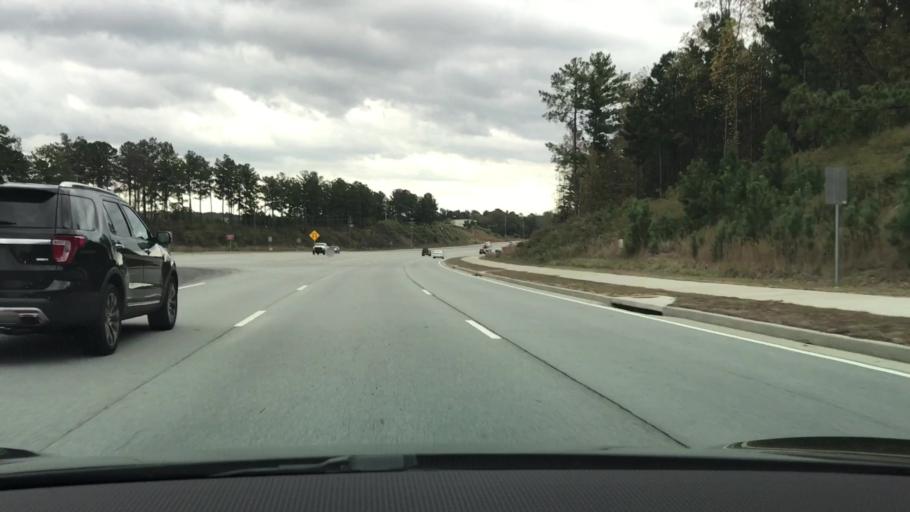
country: US
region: Georgia
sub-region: Hall County
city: Flowery Branch
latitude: 34.1312
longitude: -83.9283
